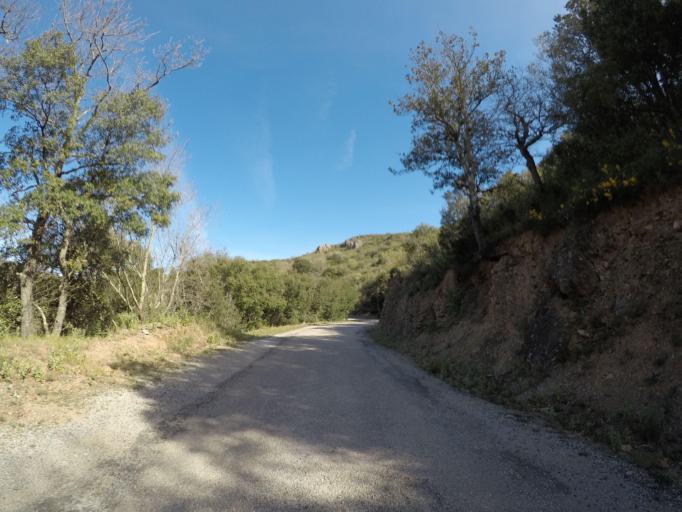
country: FR
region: Languedoc-Roussillon
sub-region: Departement des Pyrenees-Orientales
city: Thuir
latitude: 42.6277
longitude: 2.7047
